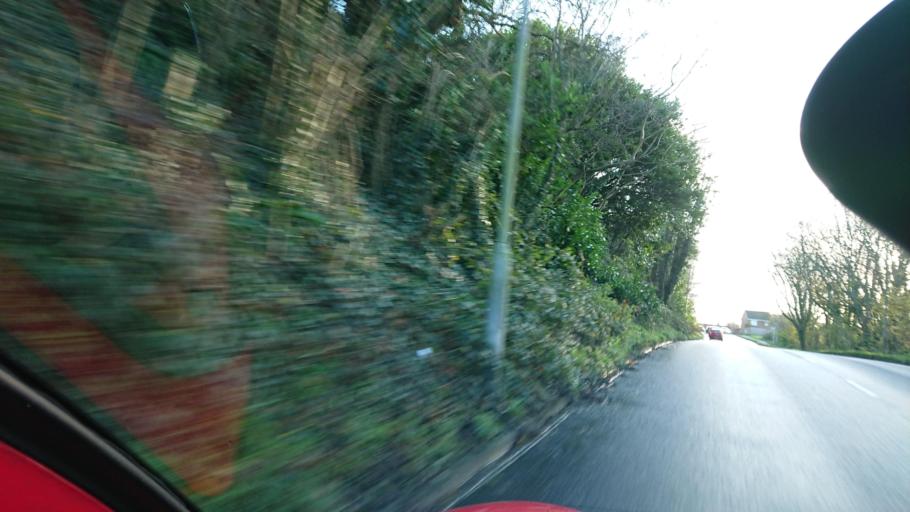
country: GB
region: England
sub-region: Plymouth
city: Plymouth
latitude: 50.4077
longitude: -4.1568
